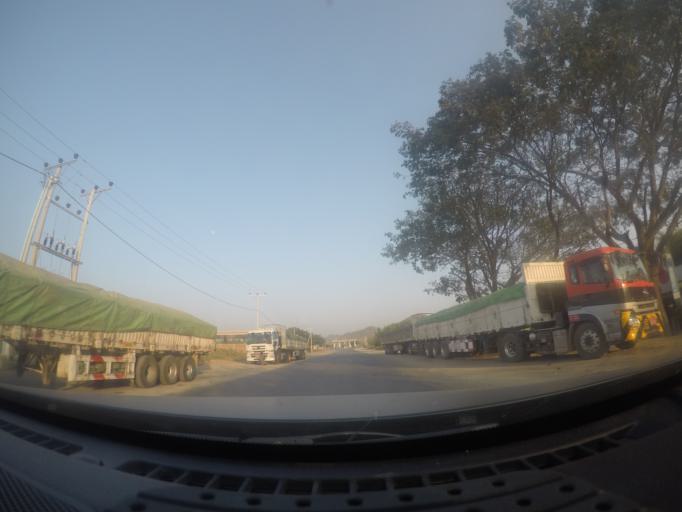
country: MM
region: Mandalay
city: Yamethin
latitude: 20.7534
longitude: 96.2579
